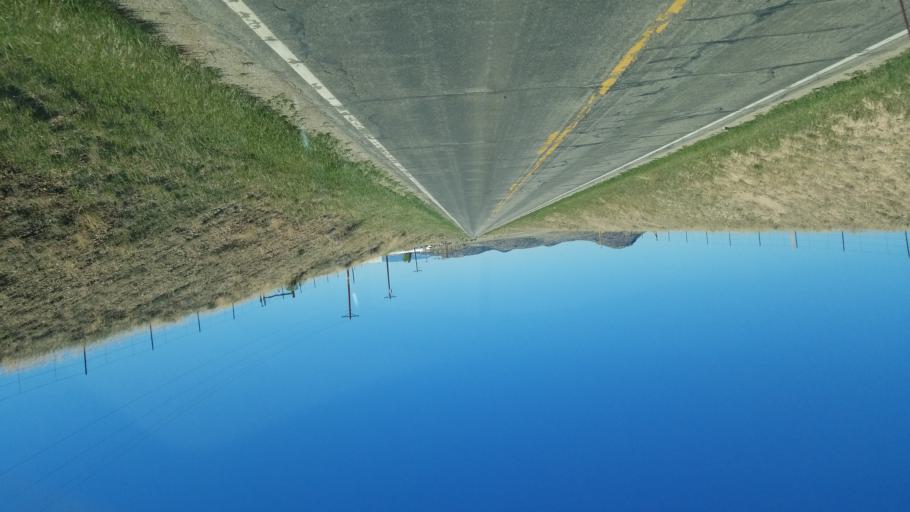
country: US
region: Colorado
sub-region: Custer County
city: Westcliffe
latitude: 38.1463
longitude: -105.4755
